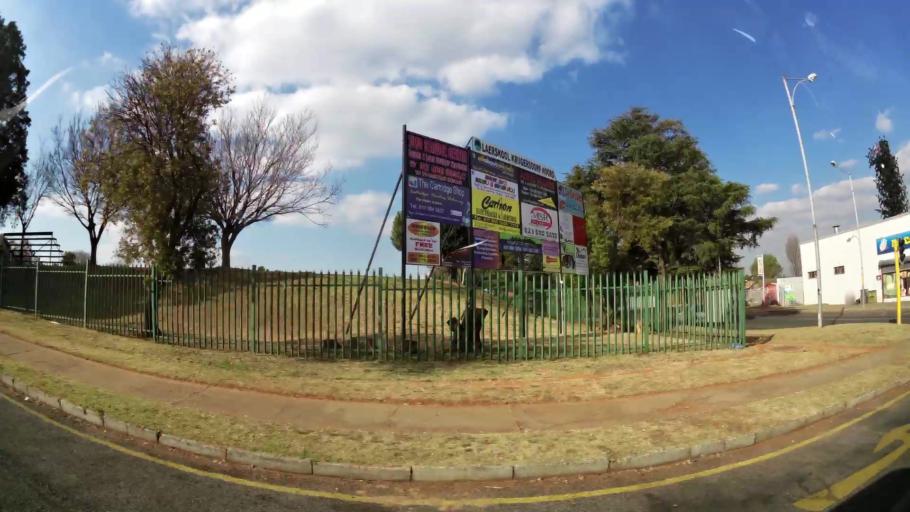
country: ZA
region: Gauteng
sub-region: West Rand District Municipality
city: Krugersdorp
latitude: -26.0911
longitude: 27.7687
